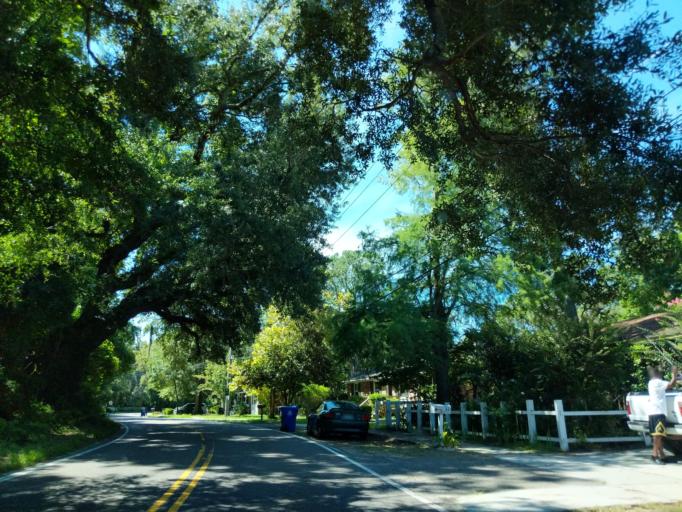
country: US
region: South Carolina
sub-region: Charleston County
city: Folly Beach
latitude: 32.7169
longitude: -79.9570
